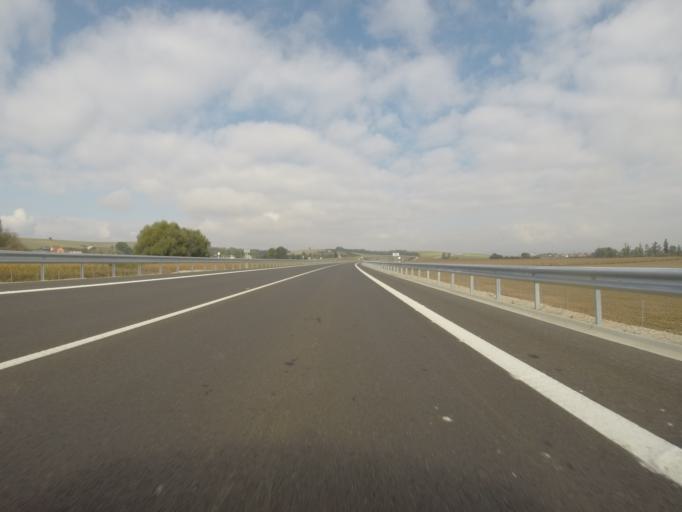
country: SK
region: Nitriansky
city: Banovce nad Bebravou
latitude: 48.7102
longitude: 18.2318
